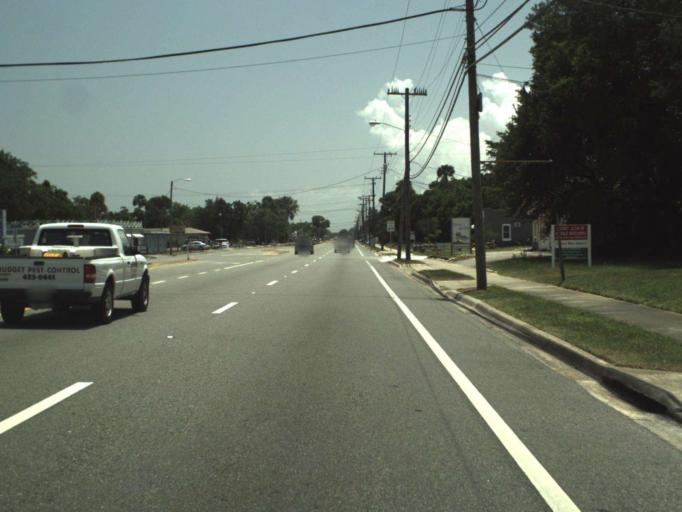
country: US
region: Florida
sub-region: Volusia County
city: Edgewater
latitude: 29.0024
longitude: -80.9132
